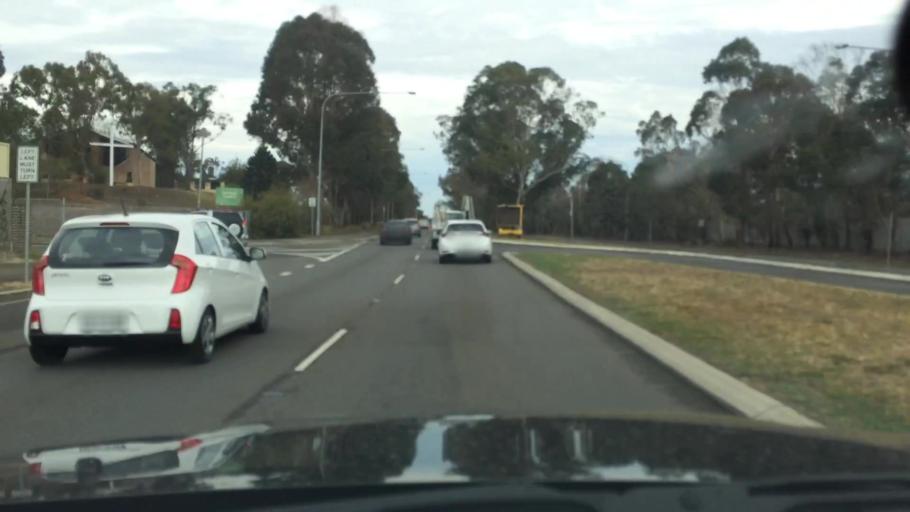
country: AU
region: New South Wales
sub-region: Fairfield
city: Cecil Park
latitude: -33.8859
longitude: 150.8629
